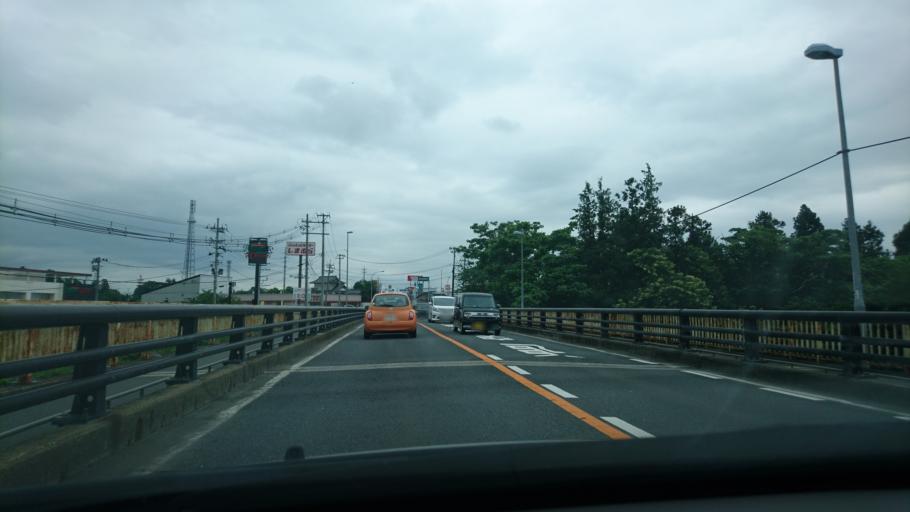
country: JP
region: Miyagi
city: Furukawa
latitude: 38.7412
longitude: 141.0182
